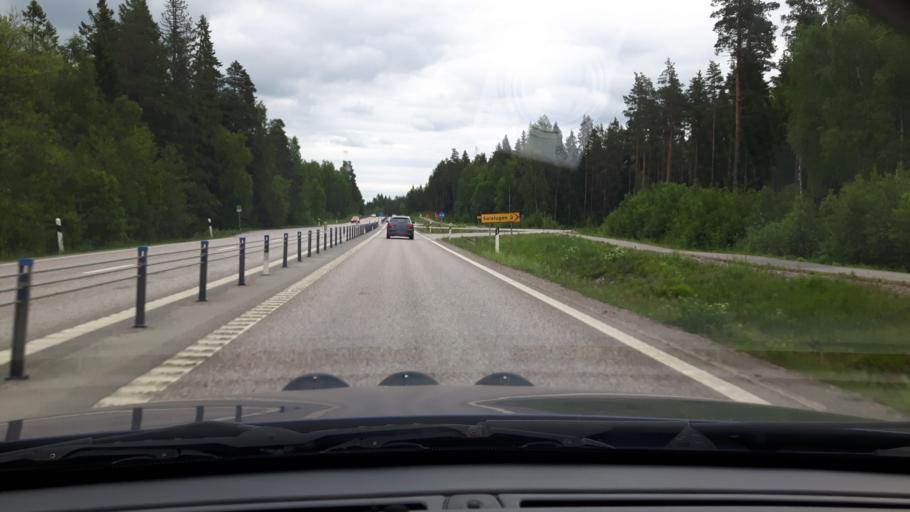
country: SE
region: Soedermanland
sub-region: Katrineholms Kommun
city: Katrineholm
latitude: 59.0114
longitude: 16.2725
